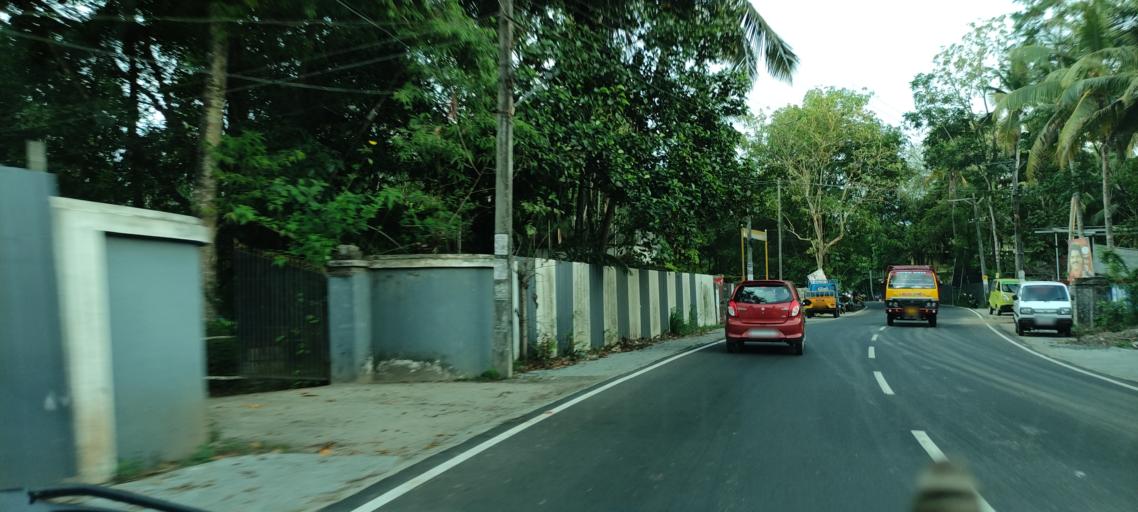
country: IN
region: Kerala
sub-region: Alappuzha
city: Arukutti
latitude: 9.8410
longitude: 76.3314
